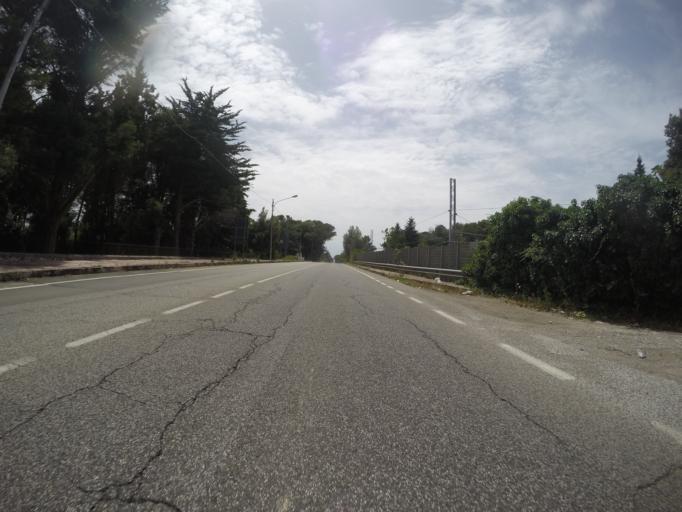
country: IT
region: Apulia
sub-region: Provincia di Taranto
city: Martina Franca
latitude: 40.6882
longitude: 17.3335
